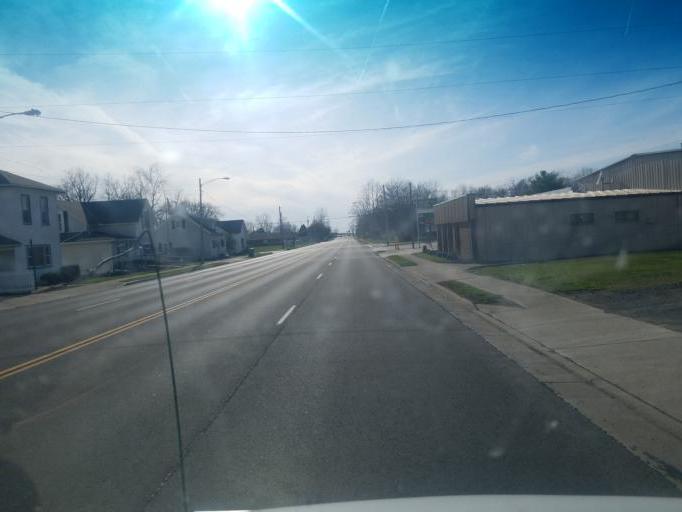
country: US
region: Ohio
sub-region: Logan County
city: Bellefontaine
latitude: 40.3633
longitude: -83.7702
